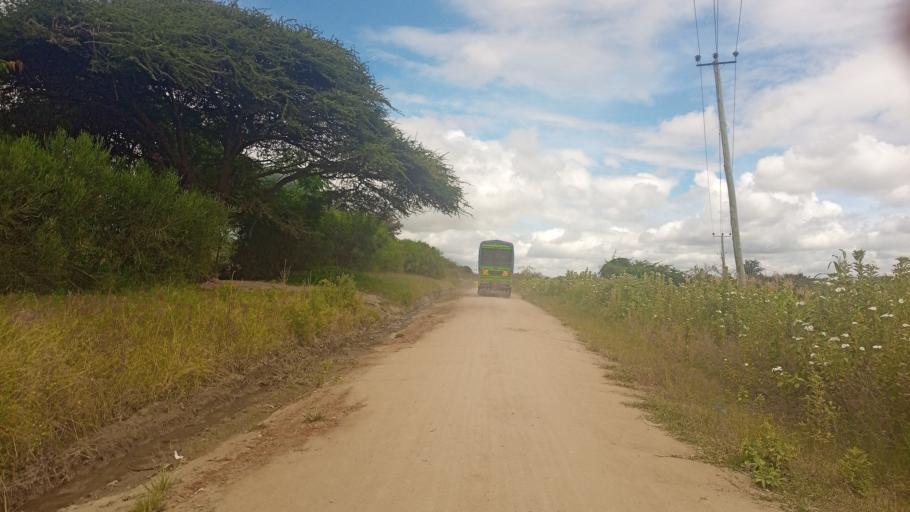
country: TZ
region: Dodoma
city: Dodoma
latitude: -6.1889
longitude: 35.7184
